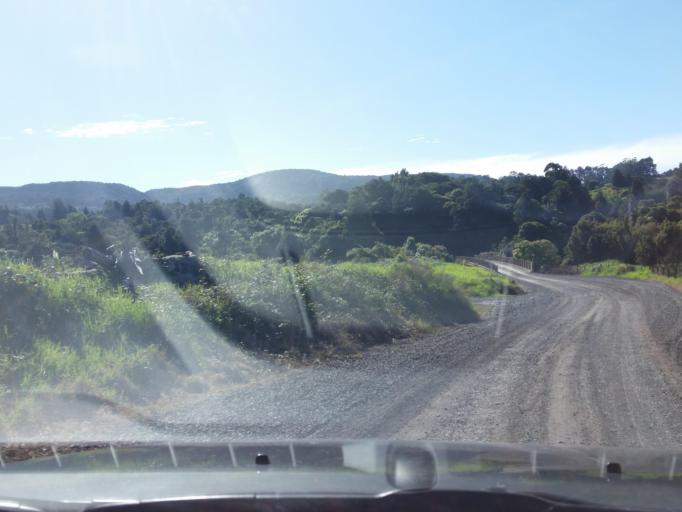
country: NZ
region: Northland
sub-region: Far North District
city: Waimate North
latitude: -35.6021
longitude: 173.7114
